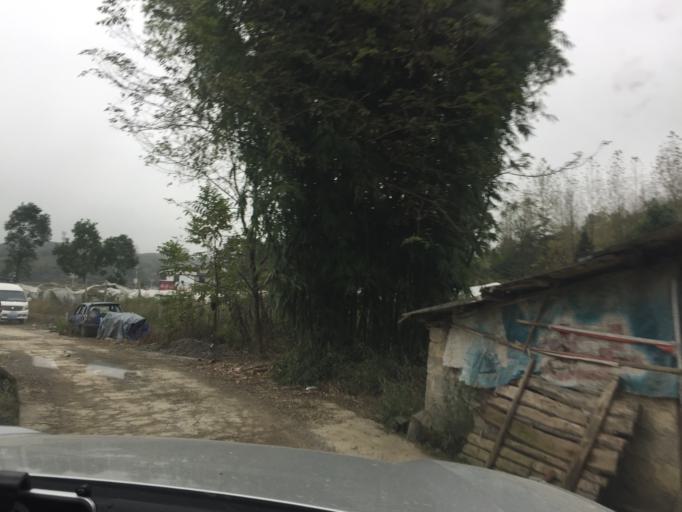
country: CN
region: Guizhou Sheng
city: Jiancha
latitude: 28.1701
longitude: 108.0047
